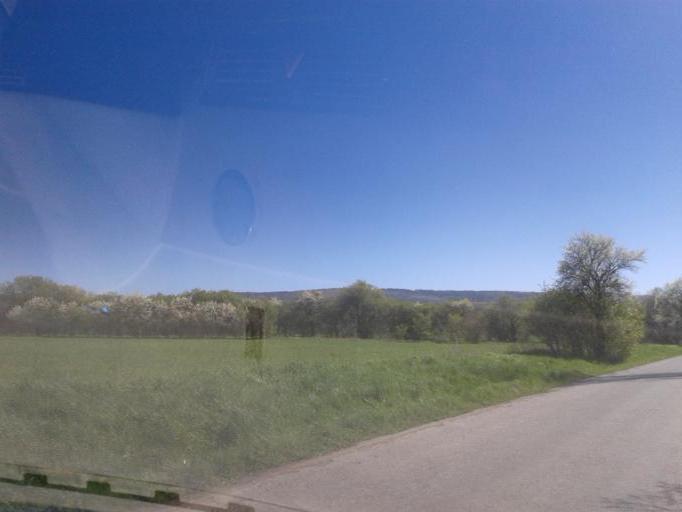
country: CZ
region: Central Bohemia
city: Revnice
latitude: 49.8838
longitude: 14.1499
